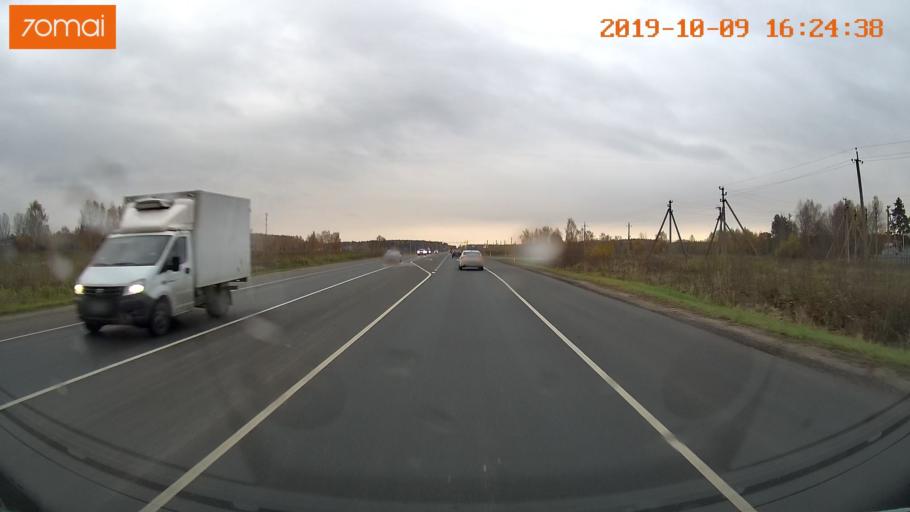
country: RU
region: Kostroma
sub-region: Kostromskoy Rayon
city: Kostroma
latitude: 57.6502
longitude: 40.9125
